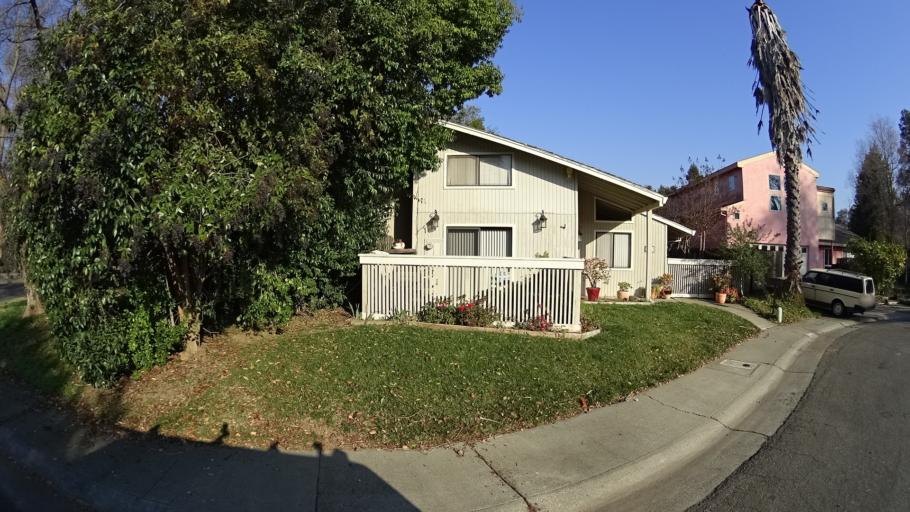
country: US
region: California
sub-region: Yolo County
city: Davis
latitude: 38.5536
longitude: -121.7930
